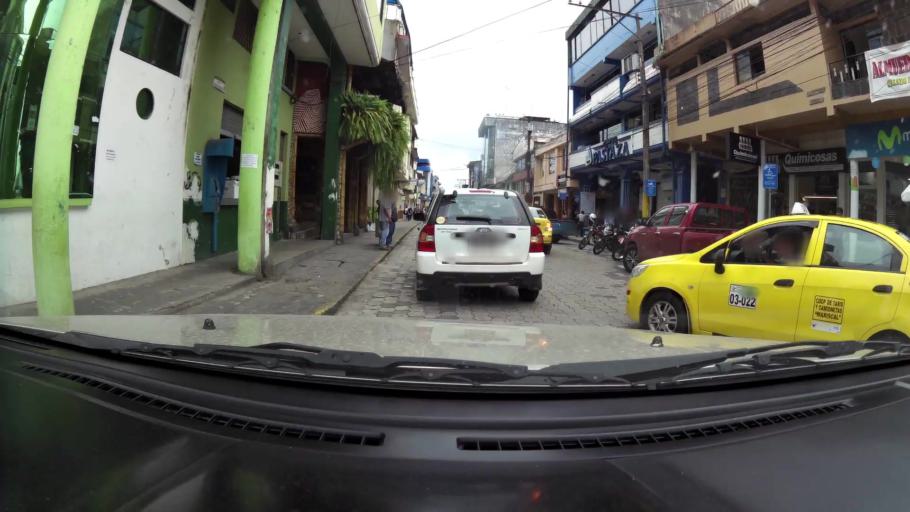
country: EC
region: Pastaza
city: Puyo
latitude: -1.4861
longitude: -77.9999
